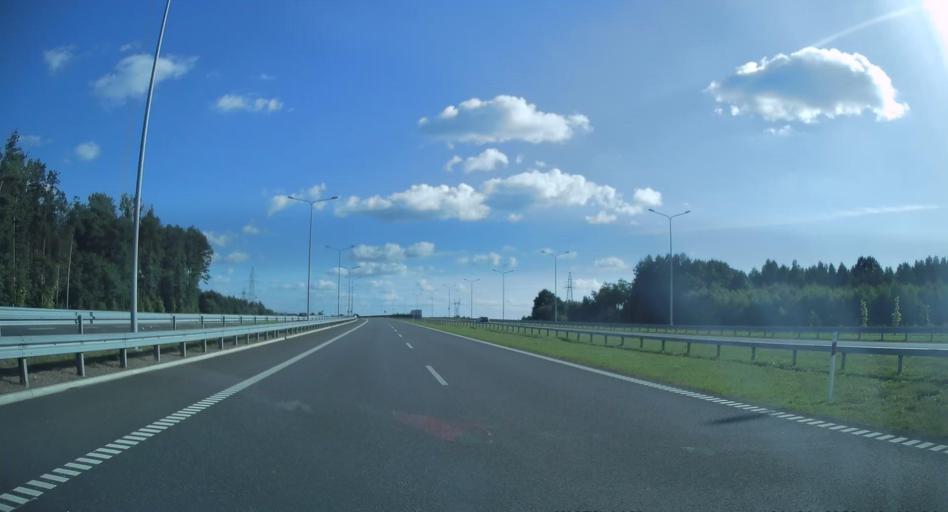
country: PL
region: Masovian Voivodeship
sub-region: Powiat szydlowiecki
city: Oronsko
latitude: 51.3402
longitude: 21.0151
